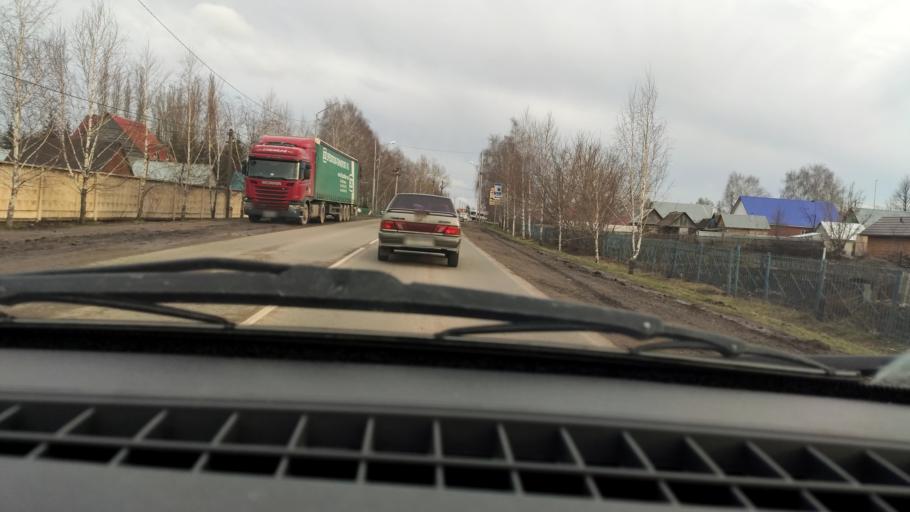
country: RU
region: Bashkortostan
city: Chishmy
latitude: 54.5967
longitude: 55.3889
